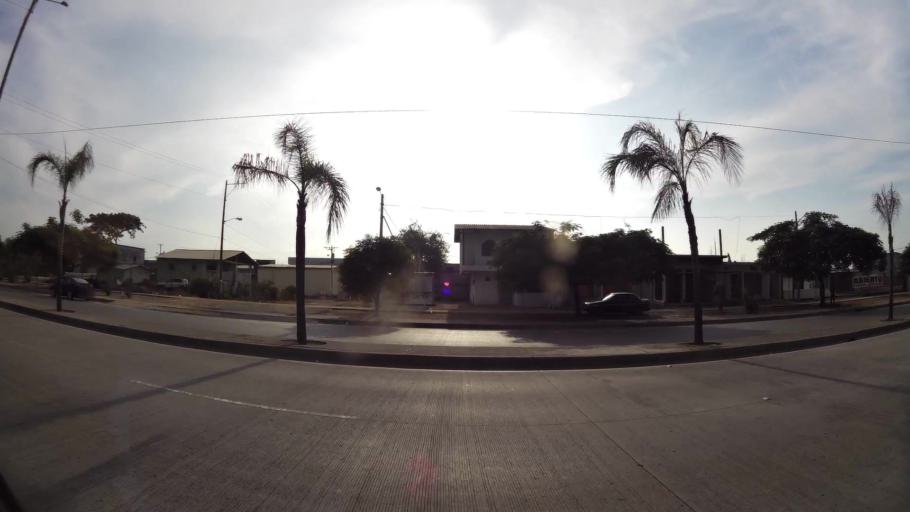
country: EC
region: Guayas
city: Eloy Alfaro
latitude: -2.0882
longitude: -79.8958
